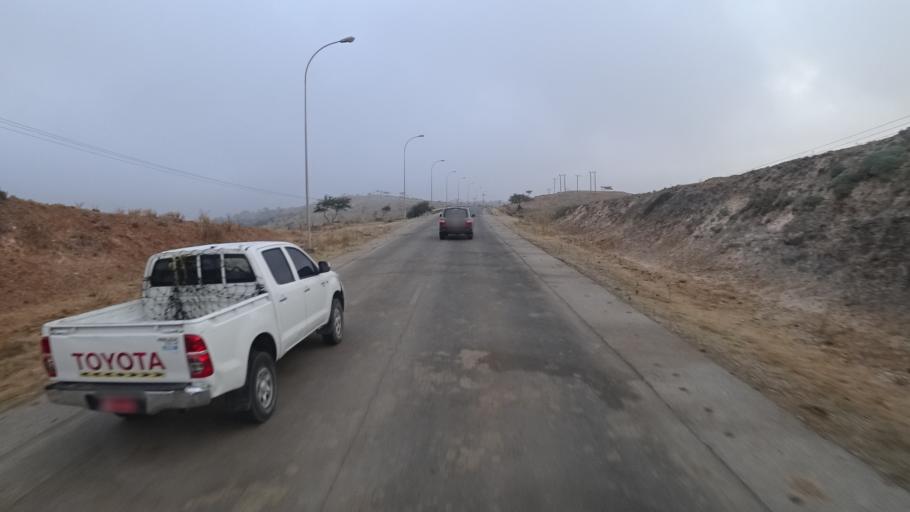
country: OM
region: Zufar
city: Salalah
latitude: 17.1335
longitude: 53.9624
